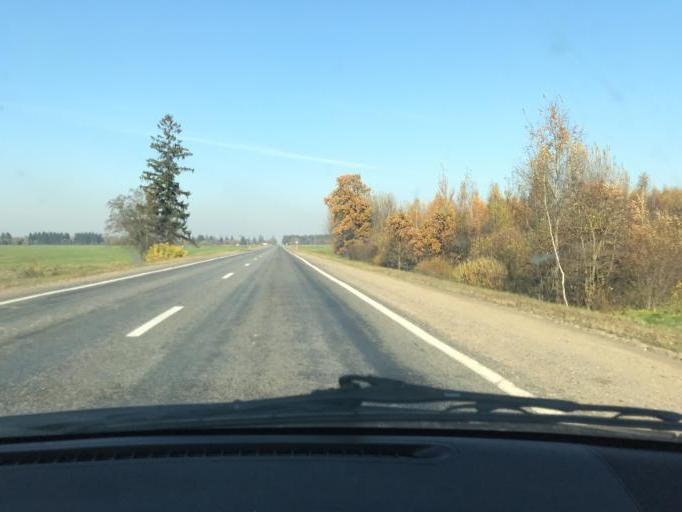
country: BY
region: Vitebsk
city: Orsha
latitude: 54.4400
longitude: 30.4853
